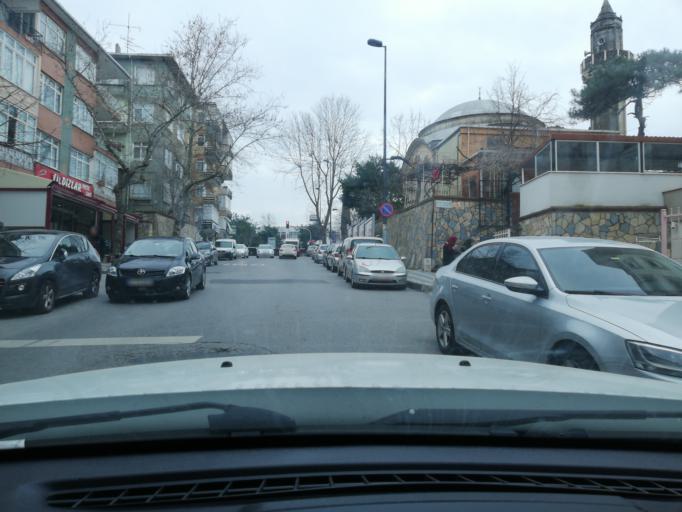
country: TR
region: Istanbul
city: UEskuedar
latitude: 41.0156
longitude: 29.0272
